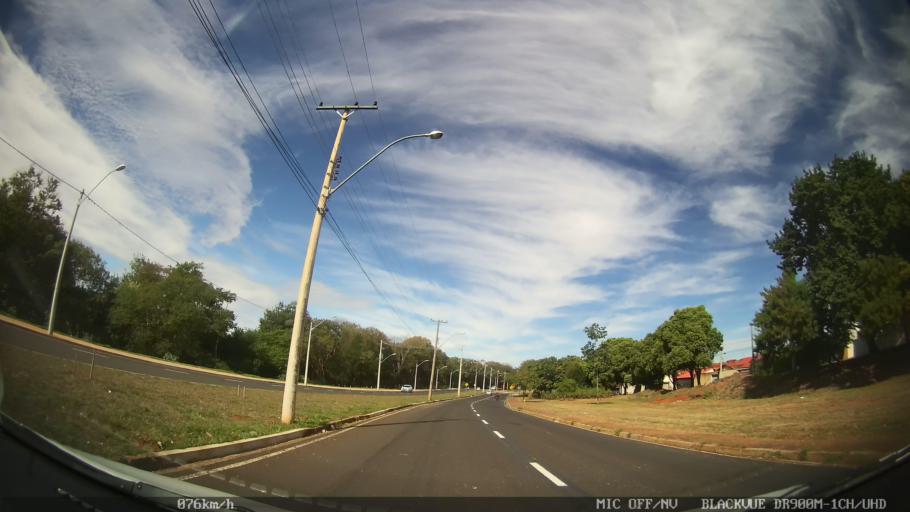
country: BR
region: Sao Paulo
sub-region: Sao Jose Do Rio Preto
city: Sao Jose do Rio Preto
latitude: -20.8364
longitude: -49.3459
